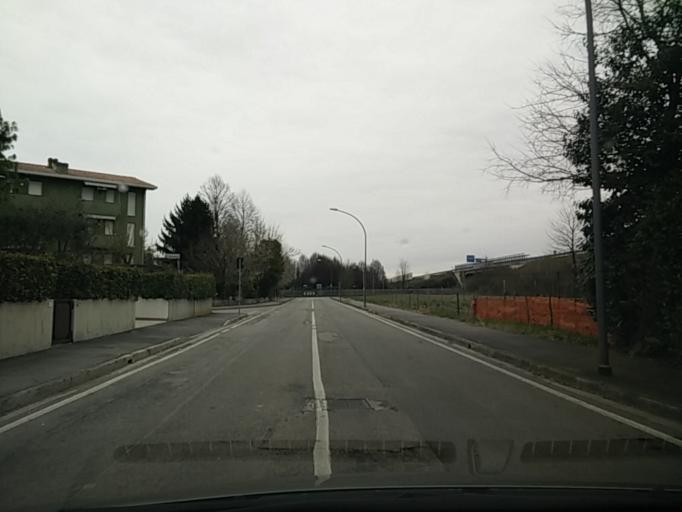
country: IT
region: Veneto
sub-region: Provincia di Treviso
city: Treviso
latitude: 45.6519
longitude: 12.2302
